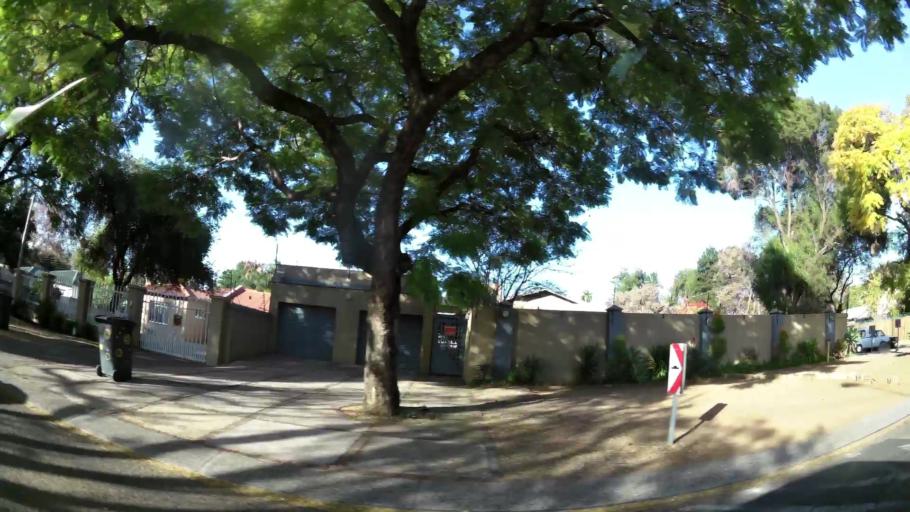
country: ZA
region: Gauteng
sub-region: City of Tshwane Metropolitan Municipality
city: Pretoria
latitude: -25.7256
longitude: 28.2131
